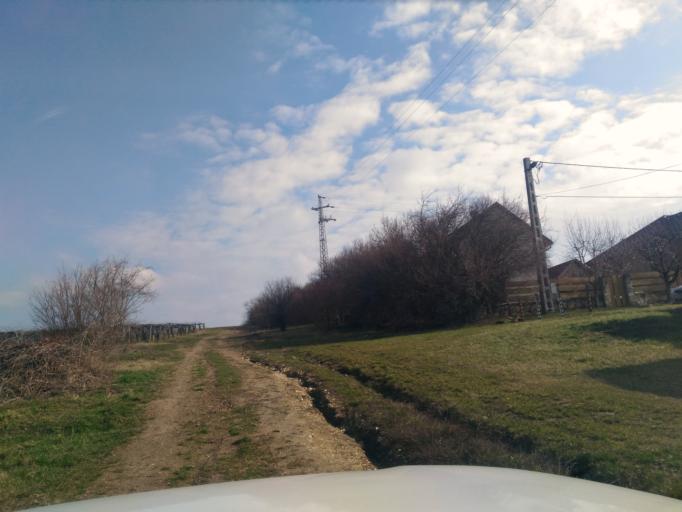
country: HU
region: Fejer
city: Etyek
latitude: 47.4525
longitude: 18.7445
